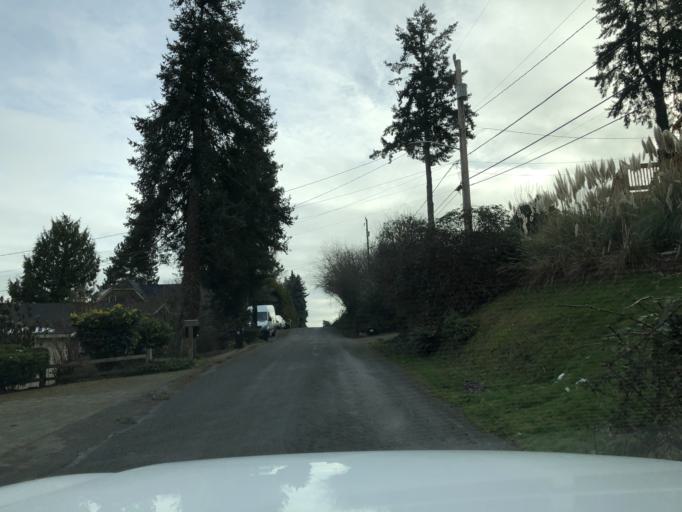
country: US
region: Washington
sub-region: King County
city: Lake Forest Park
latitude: 47.7106
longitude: -122.2783
